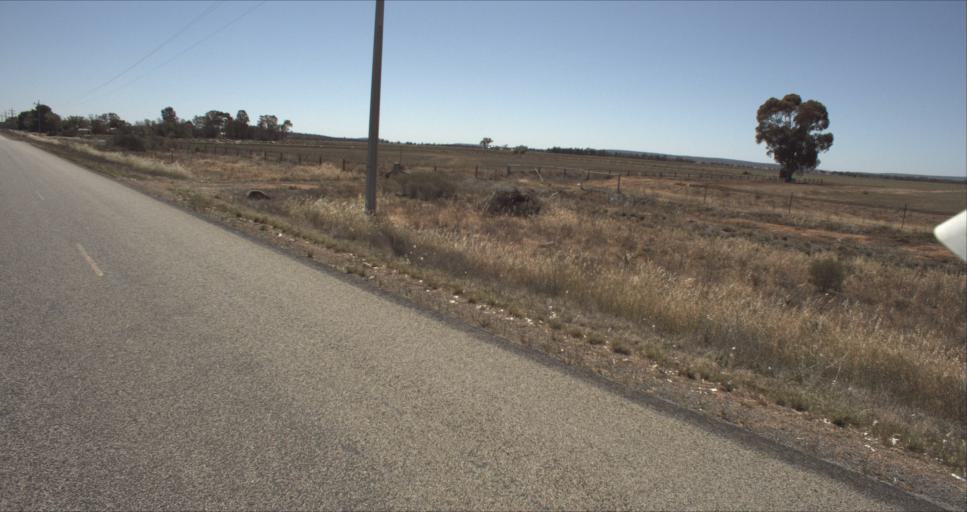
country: AU
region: New South Wales
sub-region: Leeton
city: Leeton
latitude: -34.4448
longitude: 146.2971
